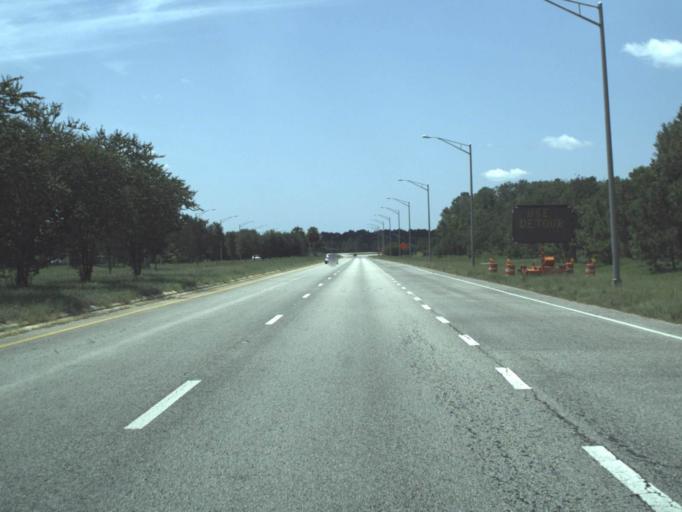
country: US
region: Florida
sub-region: Duval County
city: Jacksonville
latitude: 30.4793
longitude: -81.6646
